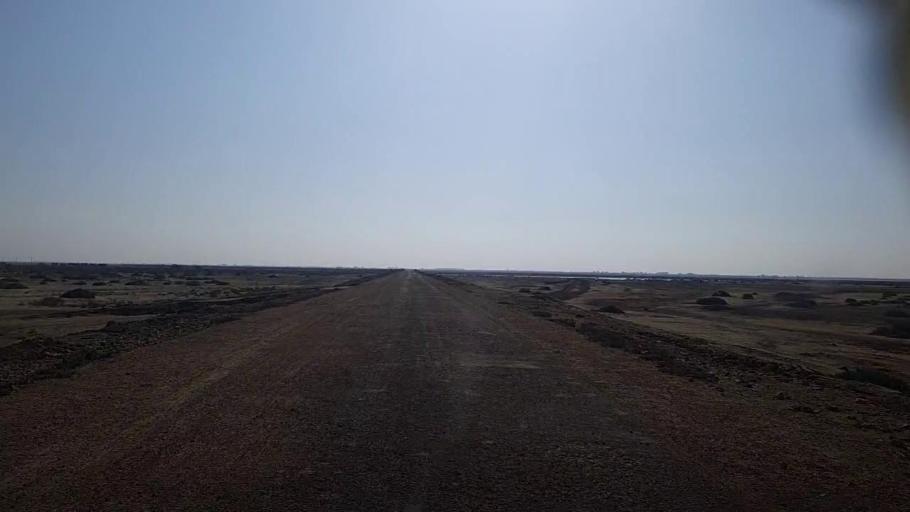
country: PK
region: Sindh
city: Mirpur Sakro
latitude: 24.5203
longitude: 67.4890
